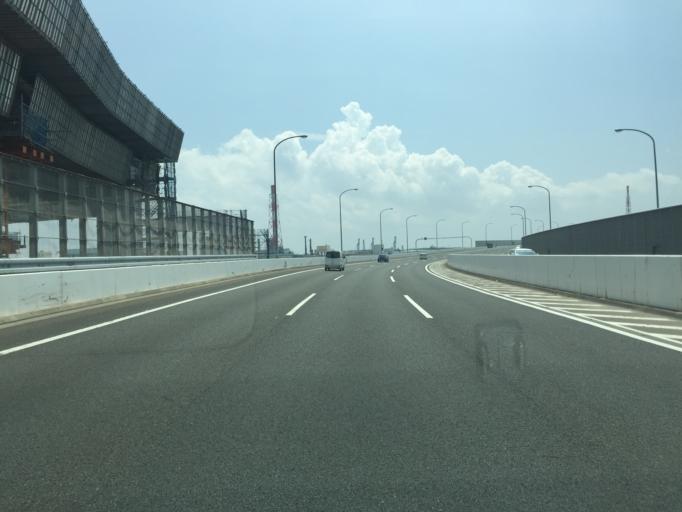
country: JP
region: Kanagawa
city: Yokohama
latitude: 35.4183
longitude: 139.6707
